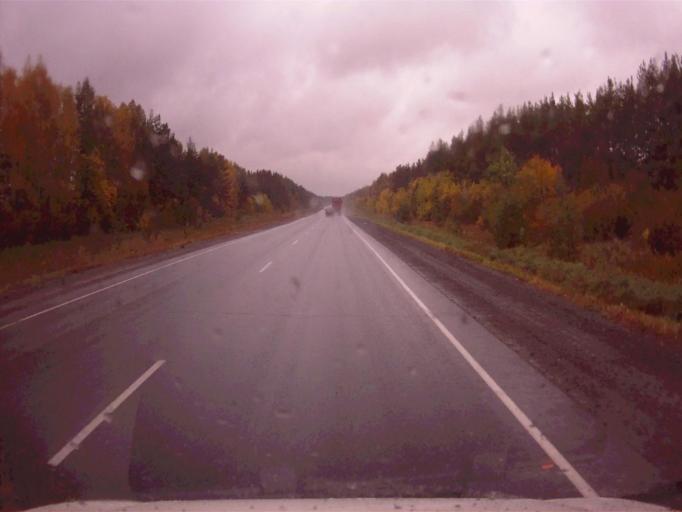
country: RU
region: Chelyabinsk
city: Roshchino
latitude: 55.3562
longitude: 61.2566
